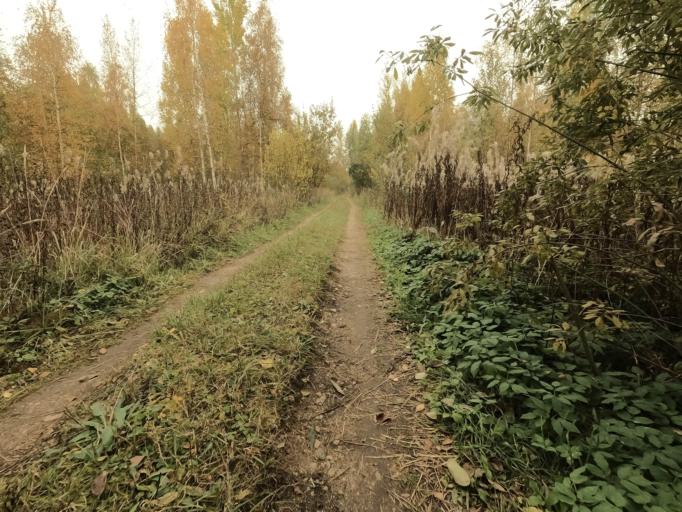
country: RU
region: Novgorod
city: Pankovka
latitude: 58.8717
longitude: 30.9373
